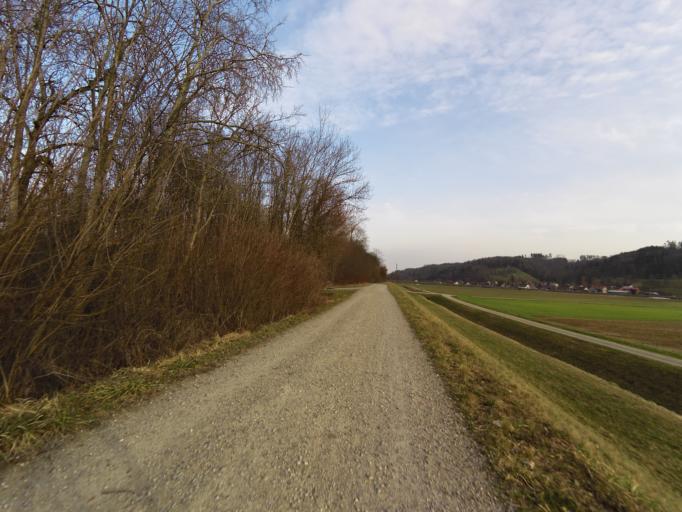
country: CH
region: Thurgau
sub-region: Frauenfeld District
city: Mullheim
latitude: 47.5849
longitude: 8.9977
